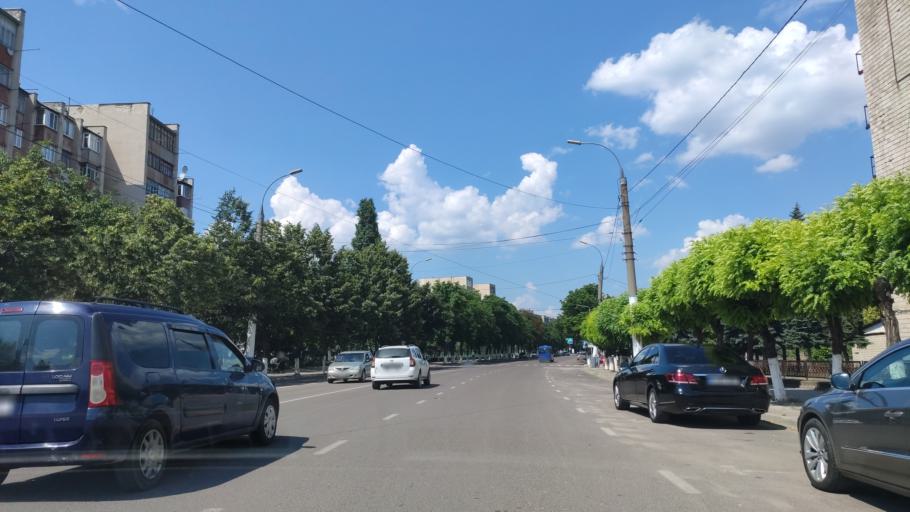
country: MD
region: Raionul Soroca
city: Soroca
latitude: 48.1577
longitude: 28.3021
